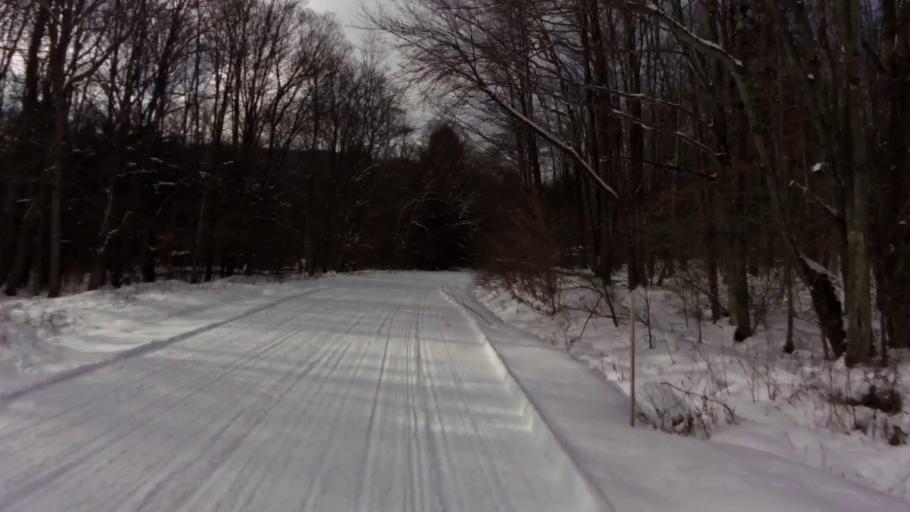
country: US
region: Pennsylvania
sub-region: McKean County
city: Bradford
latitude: 42.0246
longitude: -78.6936
